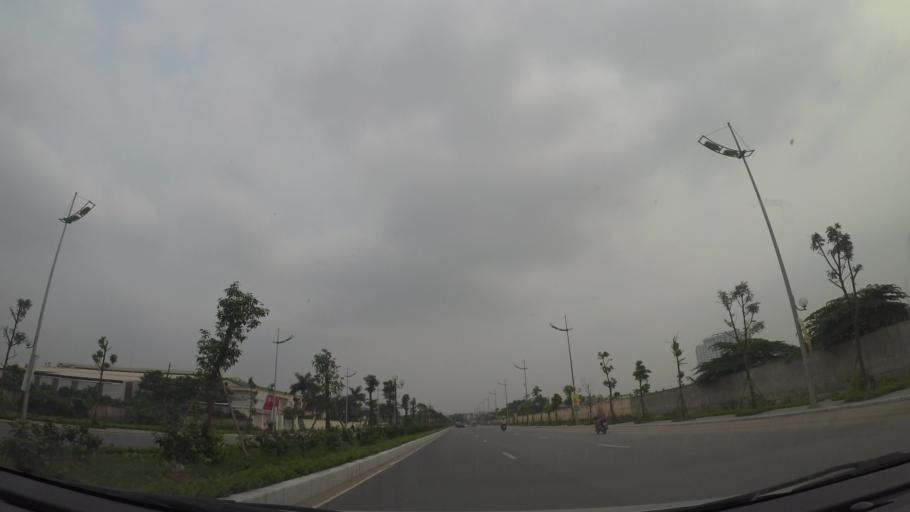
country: VN
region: Ha Noi
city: Cau Dien
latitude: 21.0456
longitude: 105.7365
